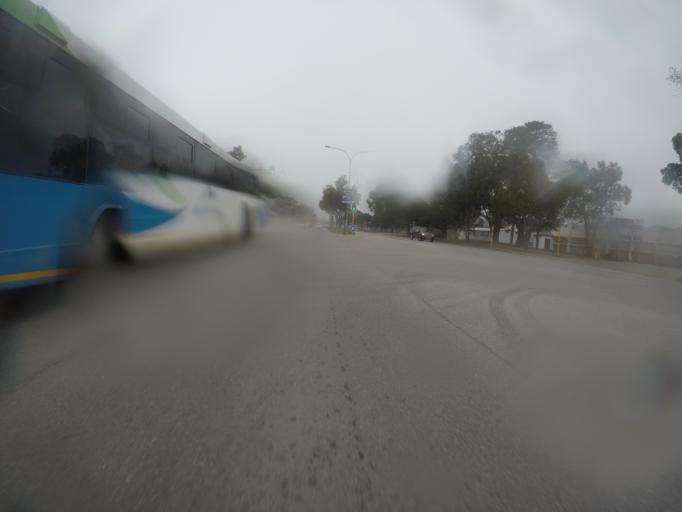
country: ZA
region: Western Cape
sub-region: Eden District Municipality
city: George
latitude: -33.9732
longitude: 22.4454
